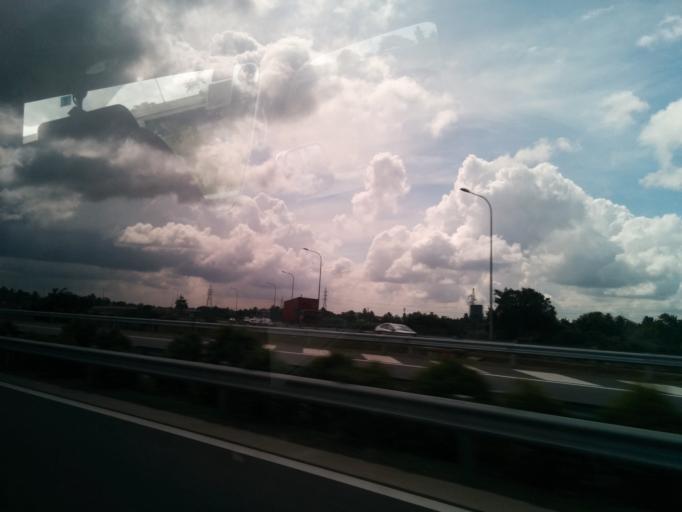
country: LK
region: Western
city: Peliyagoda
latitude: 6.9667
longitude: 79.8924
